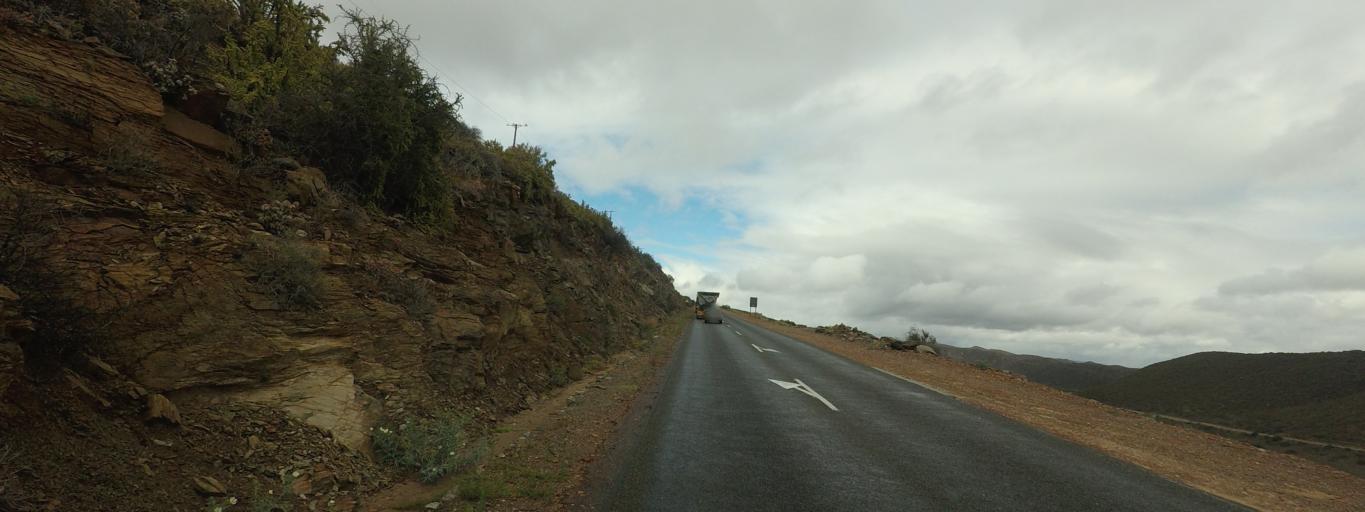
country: ZA
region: Western Cape
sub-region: Eden District Municipality
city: Oudtshoorn
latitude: -33.6866
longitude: 22.2726
